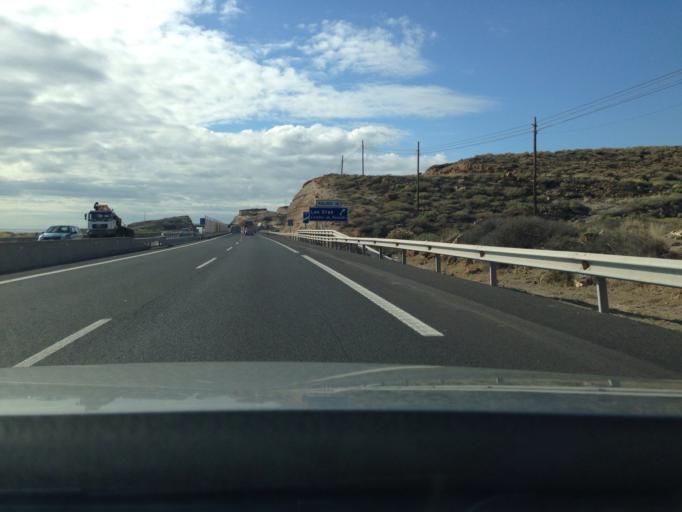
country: ES
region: Canary Islands
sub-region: Provincia de Santa Cruz de Tenerife
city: Fasnia
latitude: 28.2050
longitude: -16.4262
